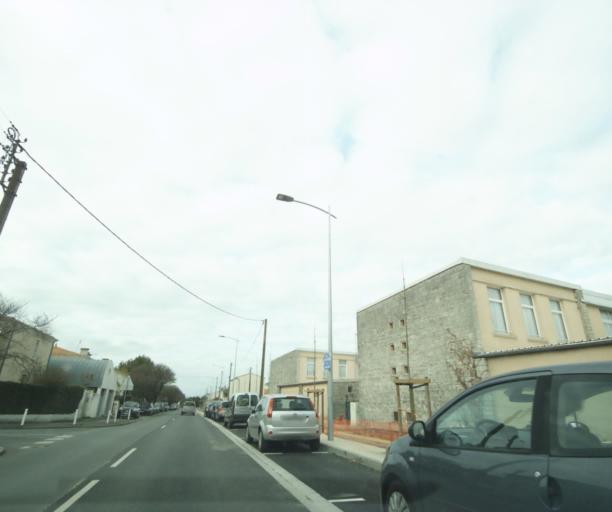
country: FR
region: Poitou-Charentes
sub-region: Departement de la Charente-Maritime
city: La Rochelle
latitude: 46.1698
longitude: -1.1638
